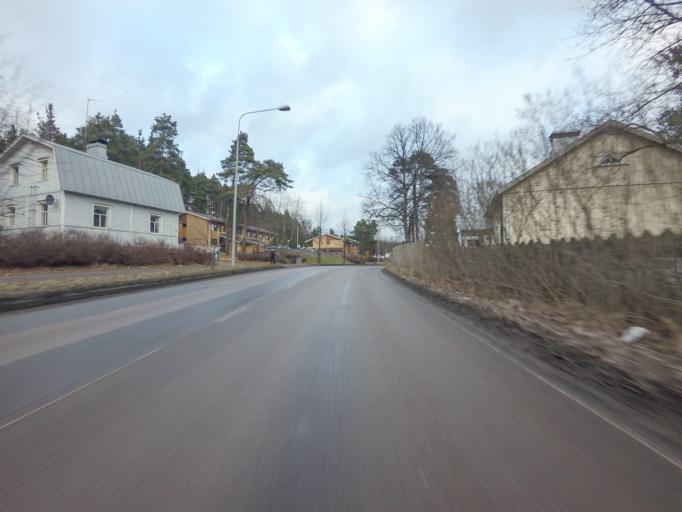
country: FI
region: Uusimaa
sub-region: Helsinki
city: Lohja
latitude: 60.2642
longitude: 24.1121
